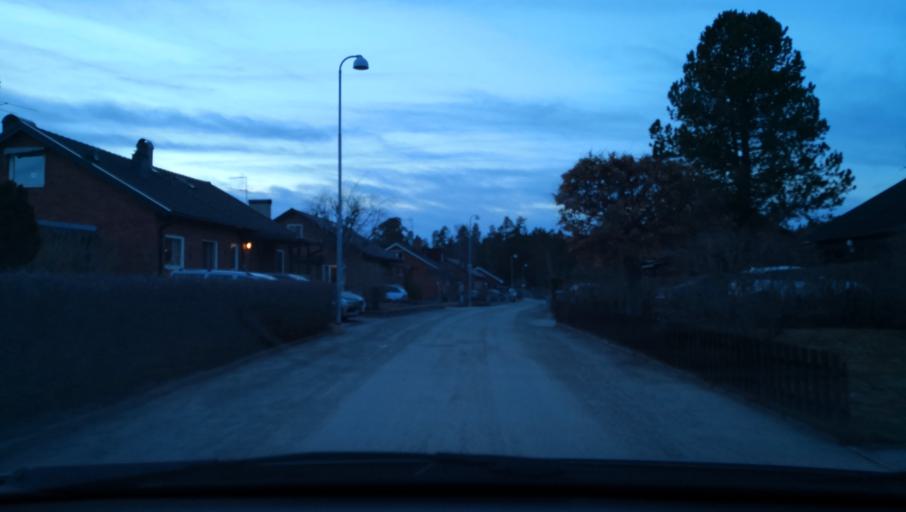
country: SE
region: Stockholm
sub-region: Varmdo Kommun
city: Gustavsberg
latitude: 59.3374
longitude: 18.3869
